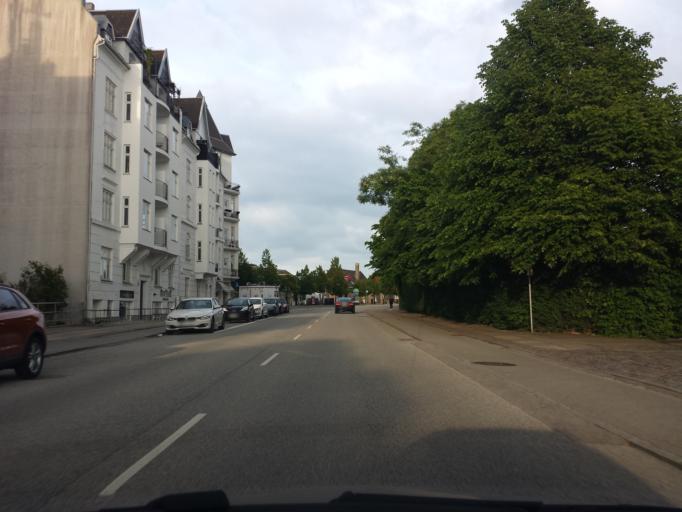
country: DK
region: Capital Region
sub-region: Lyngby-Tarbaek Kommune
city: Kongens Lyngby
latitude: 55.7535
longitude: 12.5393
